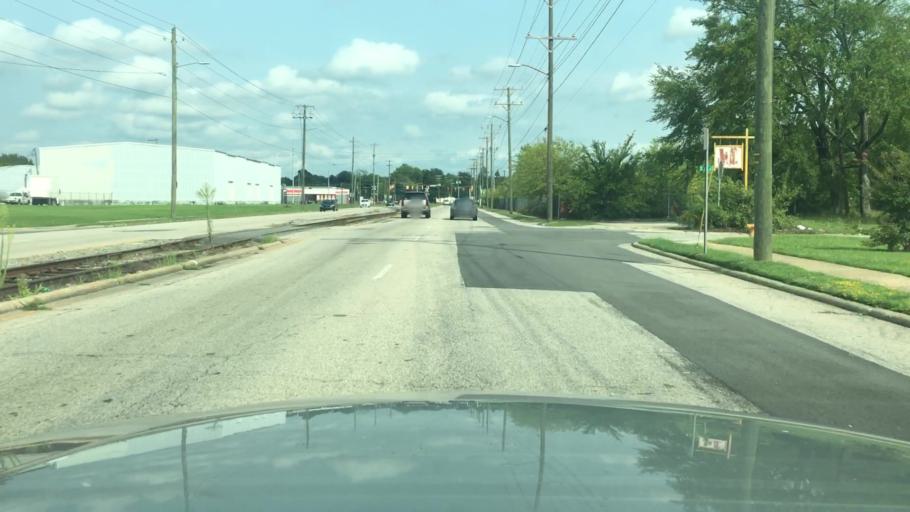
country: US
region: North Carolina
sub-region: Cumberland County
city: Fayetteville
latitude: 35.0469
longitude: -78.8686
